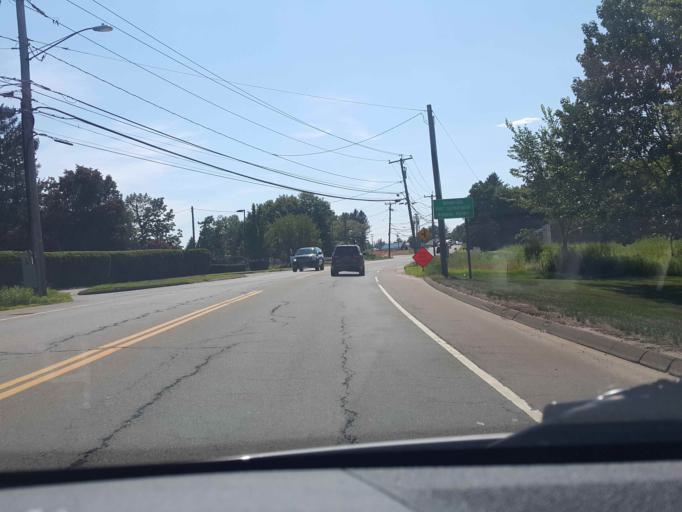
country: US
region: Connecticut
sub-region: New Haven County
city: North Branford
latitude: 41.3092
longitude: -72.7480
